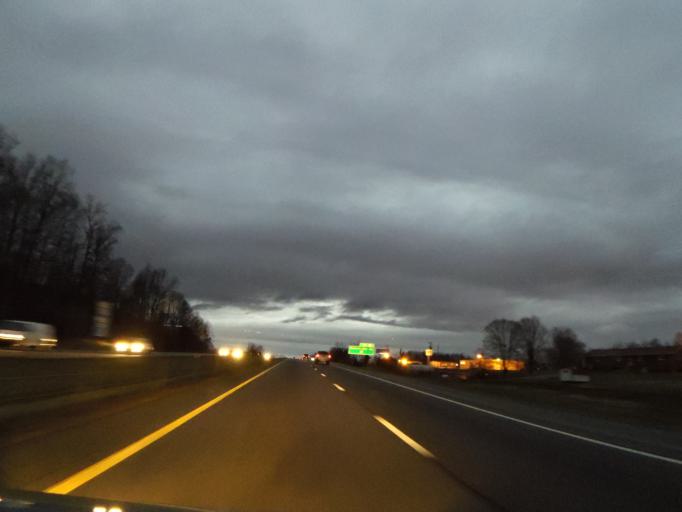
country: US
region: Tennessee
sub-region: Washington County
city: Gray
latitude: 36.4304
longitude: -82.5184
